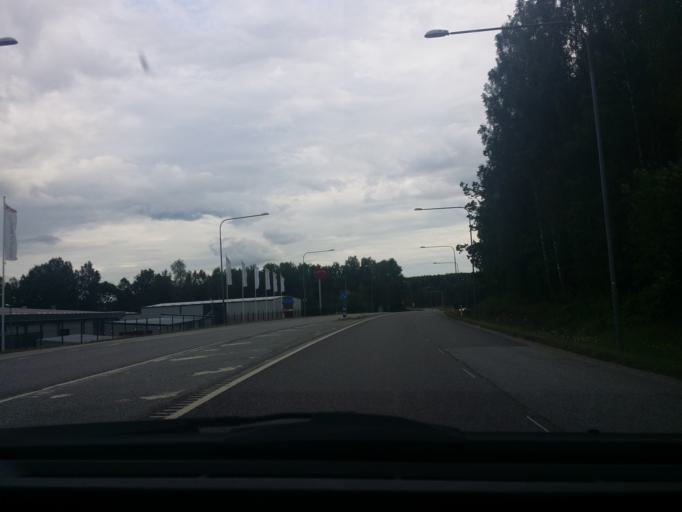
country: SE
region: OErebro
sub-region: Nora Kommun
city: Nora
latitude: 59.5112
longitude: 15.0222
